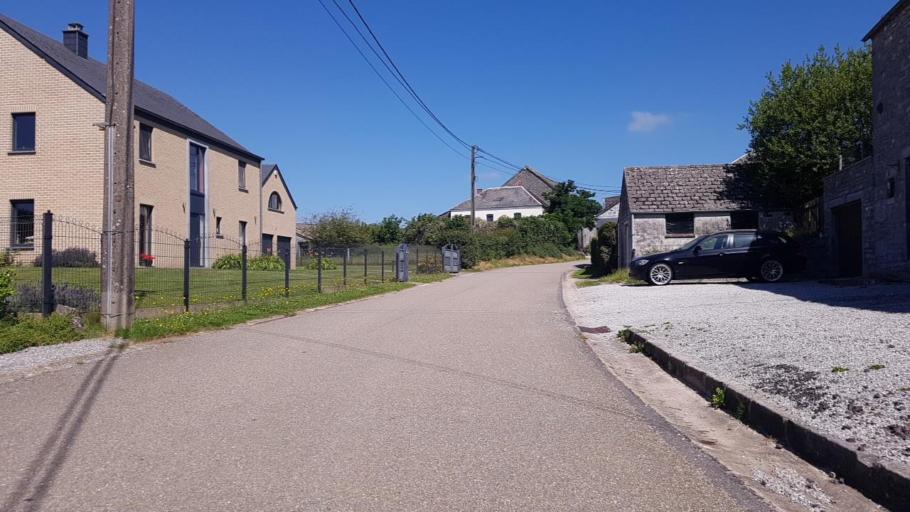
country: BE
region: Wallonia
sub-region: Province du Hainaut
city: Chimay
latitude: 50.0565
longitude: 4.2459
